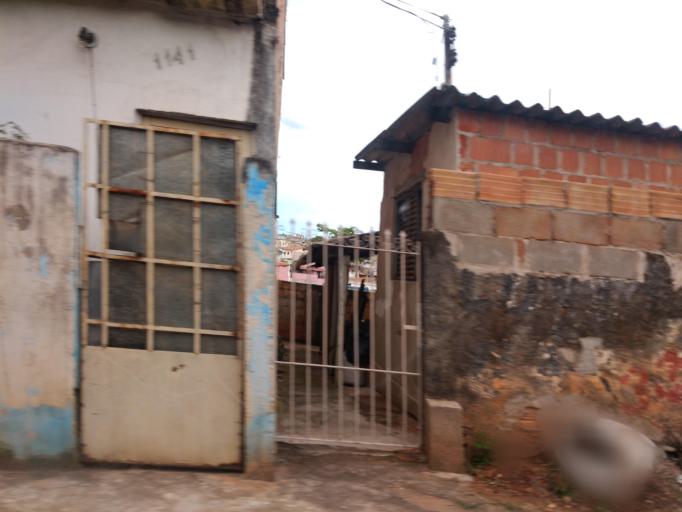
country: BR
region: Minas Gerais
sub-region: Tres Coracoes
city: Tres Coracoes
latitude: -21.6918
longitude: -45.2497
